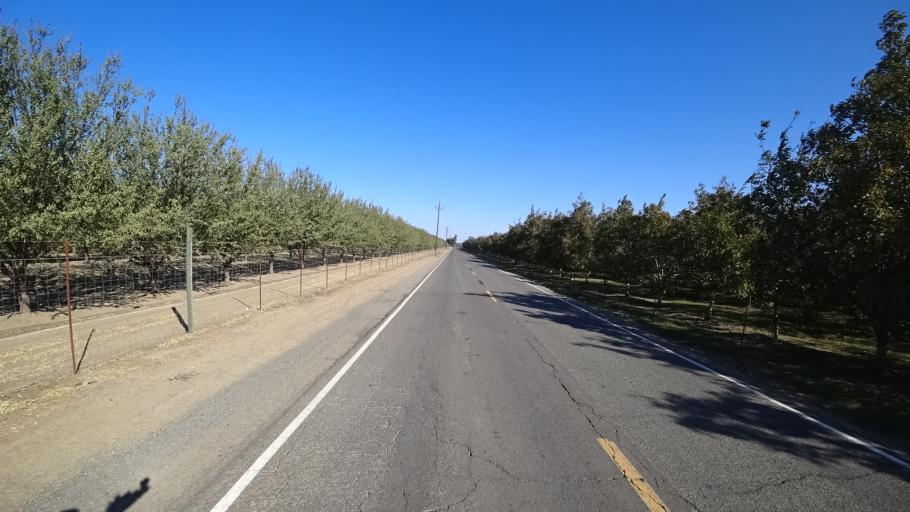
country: US
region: California
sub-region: Yolo County
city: Woodland
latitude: 38.7009
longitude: -121.8631
